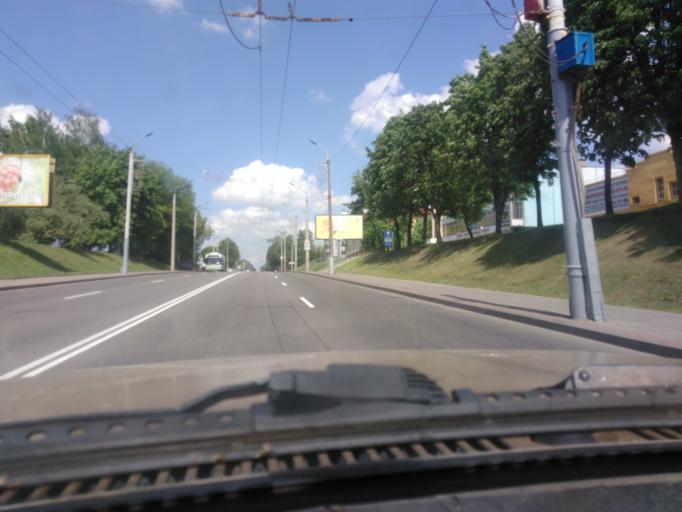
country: BY
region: Mogilev
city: Mahilyow
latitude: 53.9233
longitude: 30.3419
